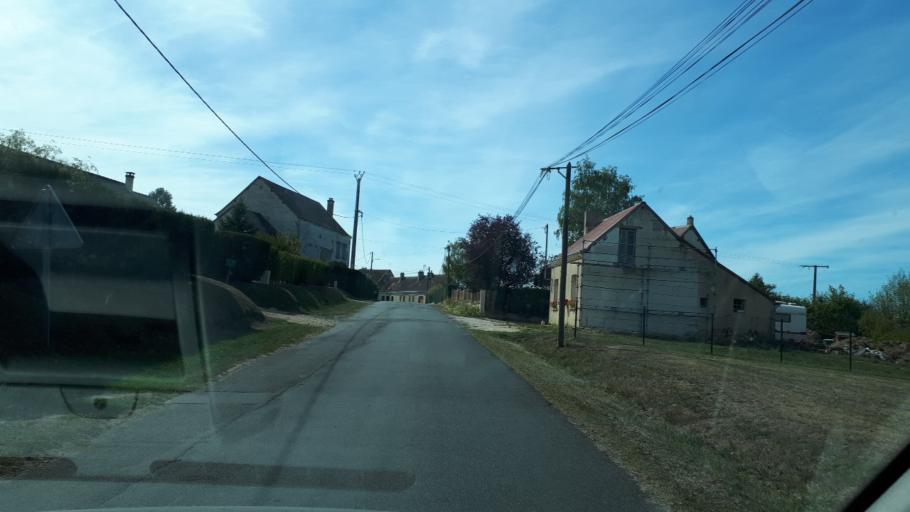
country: FR
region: Centre
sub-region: Departement du Loir-et-Cher
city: Montoire-sur-le-Loir
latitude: 47.7247
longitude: 0.8281
